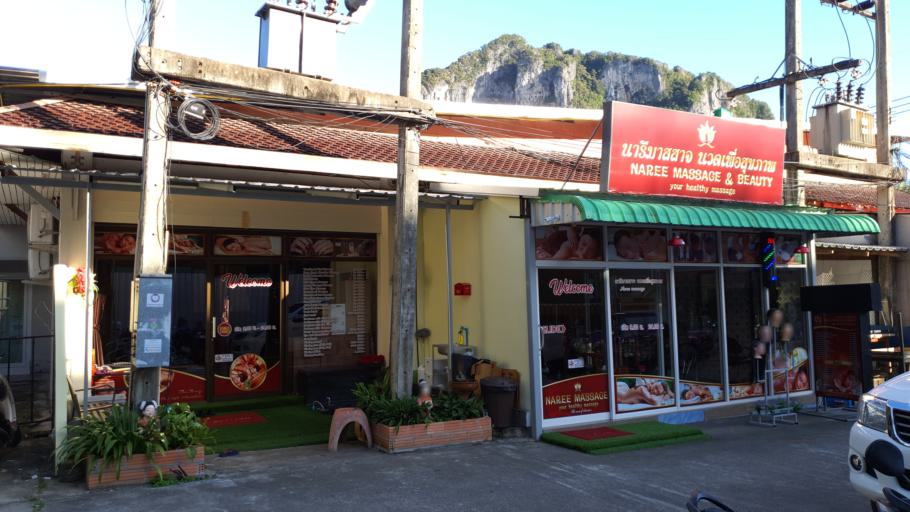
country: TH
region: Phangnga
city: Ban Ao Nang
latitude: 8.0327
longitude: 98.8238
